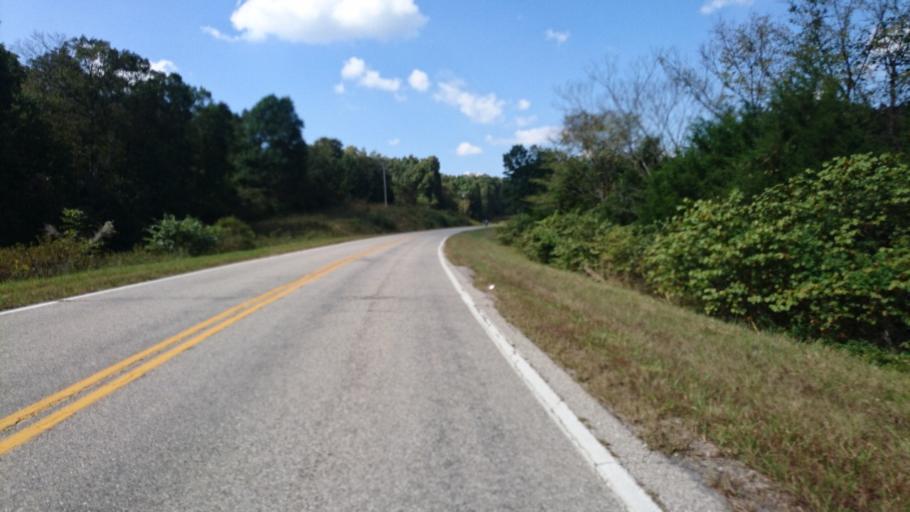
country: US
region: Missouri
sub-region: Pulaski County
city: Richland
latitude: 37.7523
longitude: -92.4987
